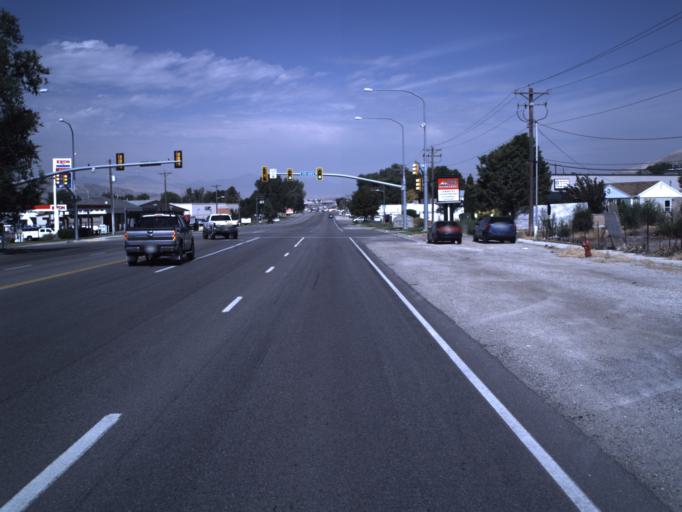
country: US
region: Utah
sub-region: Utah County
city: Lehi
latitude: 40.4058
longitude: -111.8596
